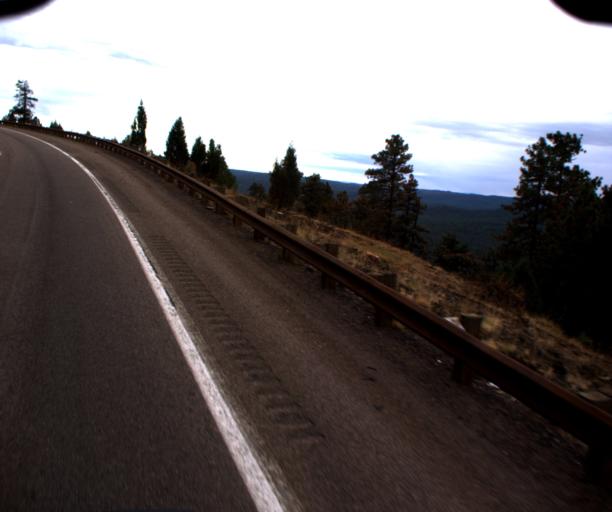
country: US
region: Arizona
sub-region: Gila County
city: Star Valley
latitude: 34.3037
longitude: -110.9200
